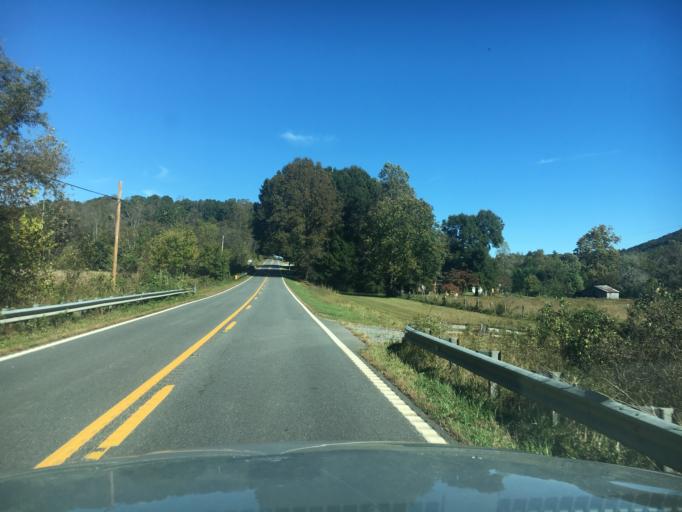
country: US
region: North Carolina
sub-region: Rutherford County
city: Spindale
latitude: 35.5052
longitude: -81.8566
